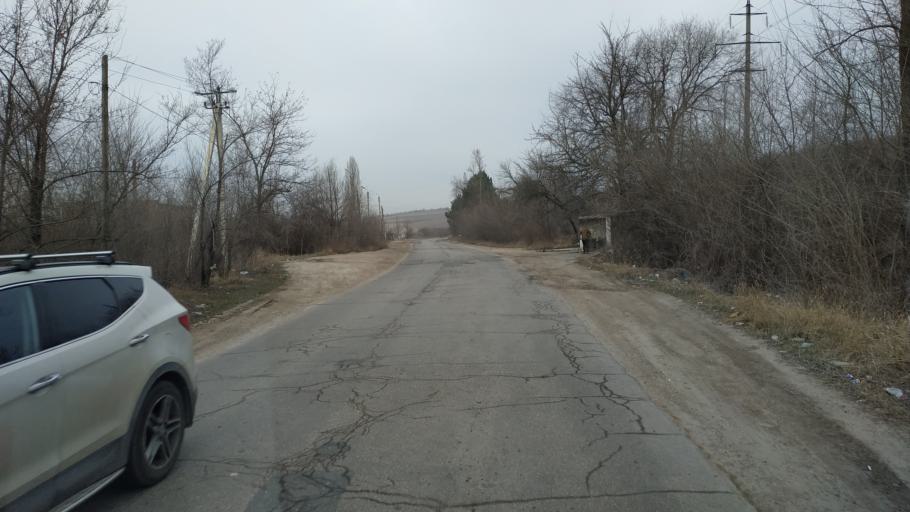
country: MD
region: Chisinau
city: Vatra
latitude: 47.0714
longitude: 28.7734
